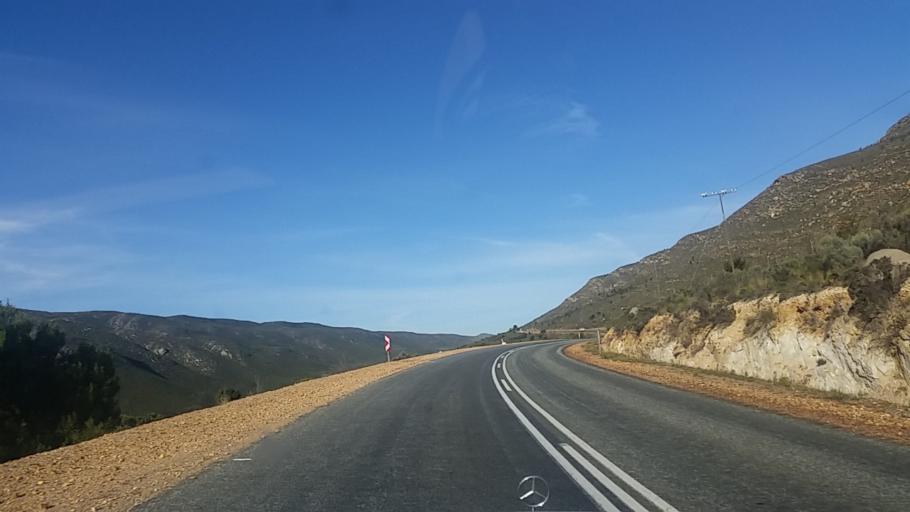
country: ZA
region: Western Cape
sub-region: Eden District Municipality
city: Knysna
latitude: -33.7502
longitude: 22.9639
